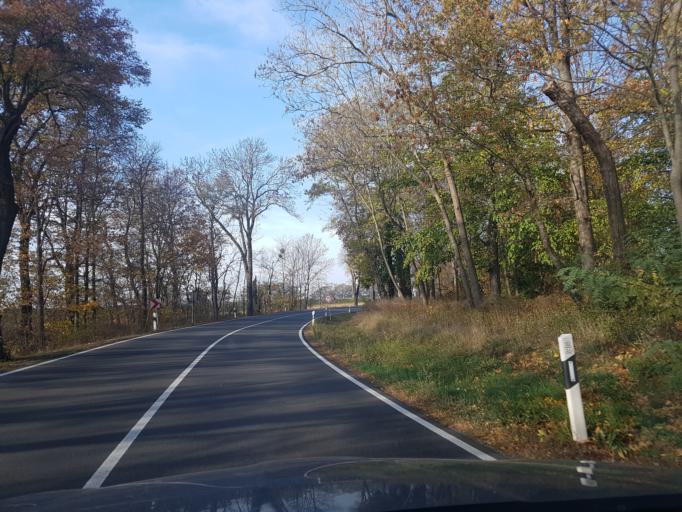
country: DE
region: Saxony
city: Beilrode
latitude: 51.5441
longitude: 13.0545
